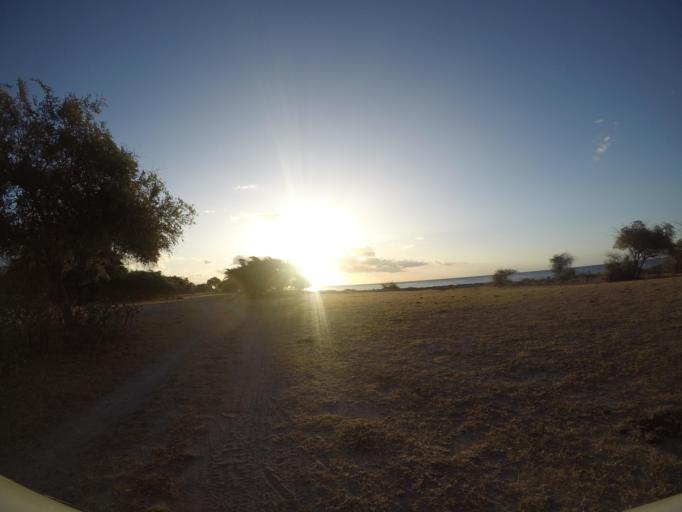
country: TL
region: Lautem
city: Lospalos
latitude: -8.3231
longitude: 126.9980
